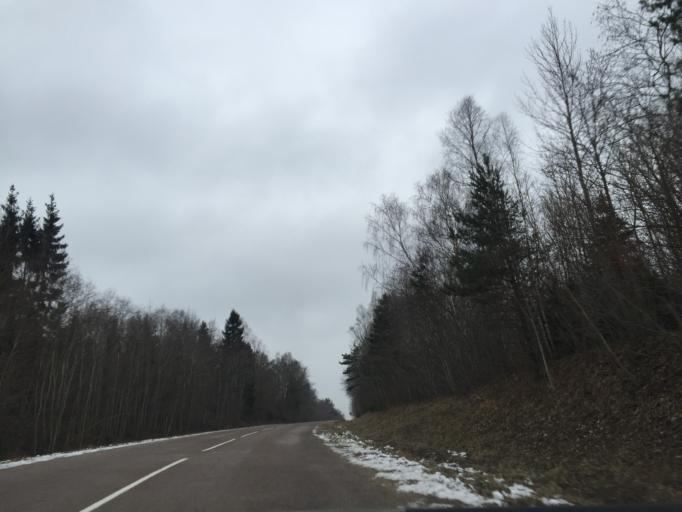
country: EE
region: Saare
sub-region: Kuressaare linn
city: Kuressaare
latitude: 58.3658
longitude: 22.2307
